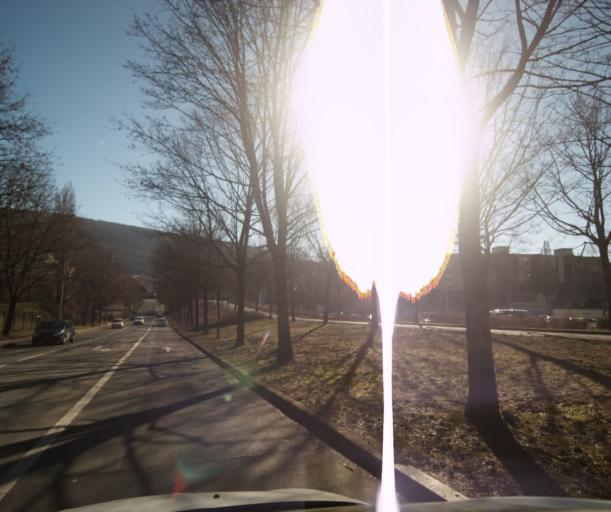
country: FR
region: Franche-Comte
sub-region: Departement du Doubs
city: Avanne-Aveney
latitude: 47.2191
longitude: 5.9757
